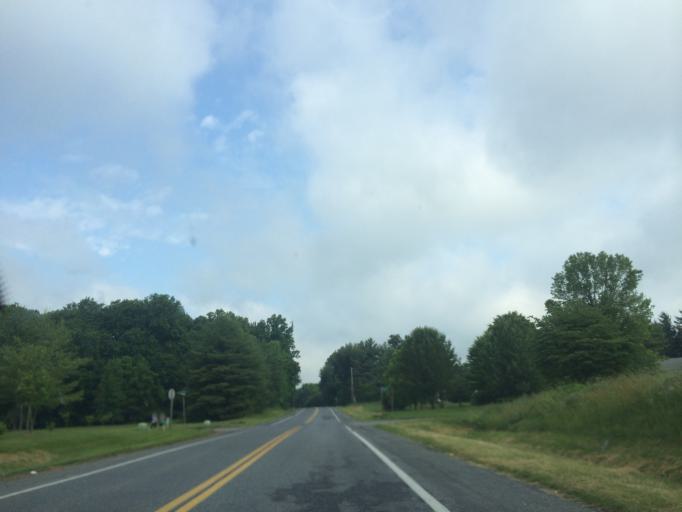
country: US
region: Maryland
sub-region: Howard County
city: Fulton
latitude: 39.1653
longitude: -76.9088
